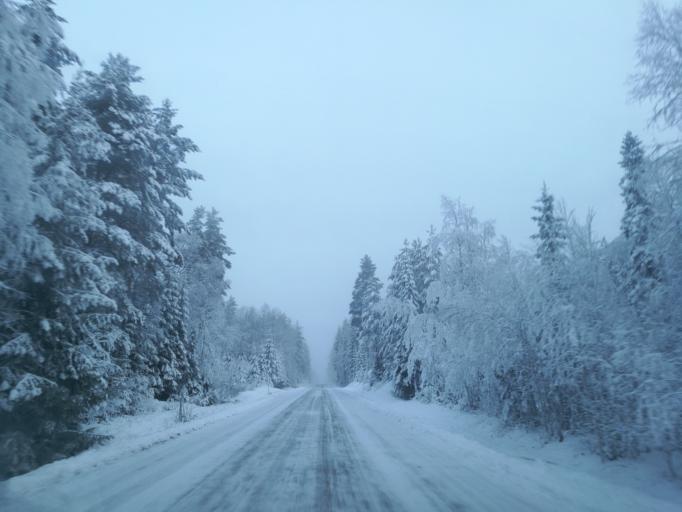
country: NO
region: Hedmark
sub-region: Grue
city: Kirkenaer
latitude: 60.4705
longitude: 12.5492
